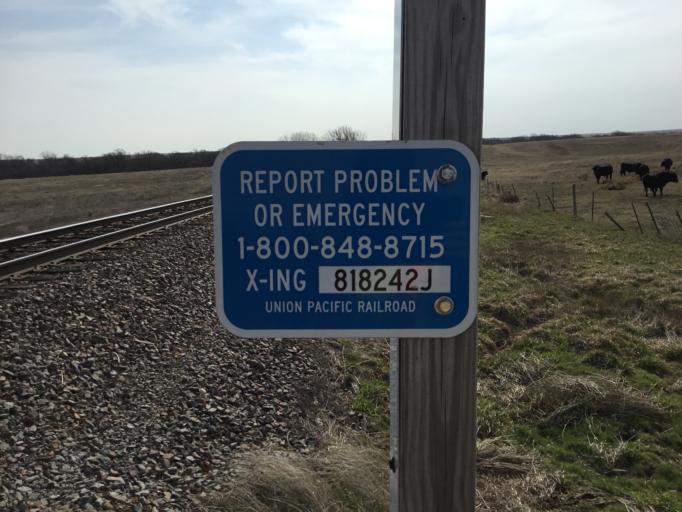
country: US
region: Kansas
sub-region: Ellsworth County
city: Ellsworth
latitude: 38.7322
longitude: -98.0953
